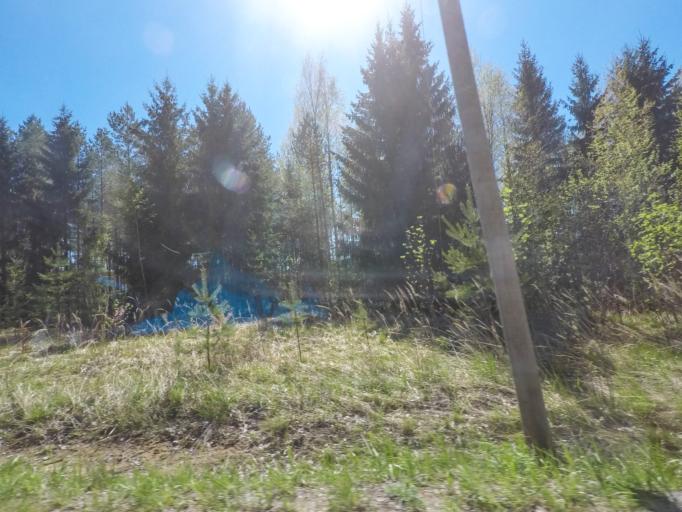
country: FI
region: Uusimaa
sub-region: Helsinki
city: Sammatti
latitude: 60.3334
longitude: 23.8054
